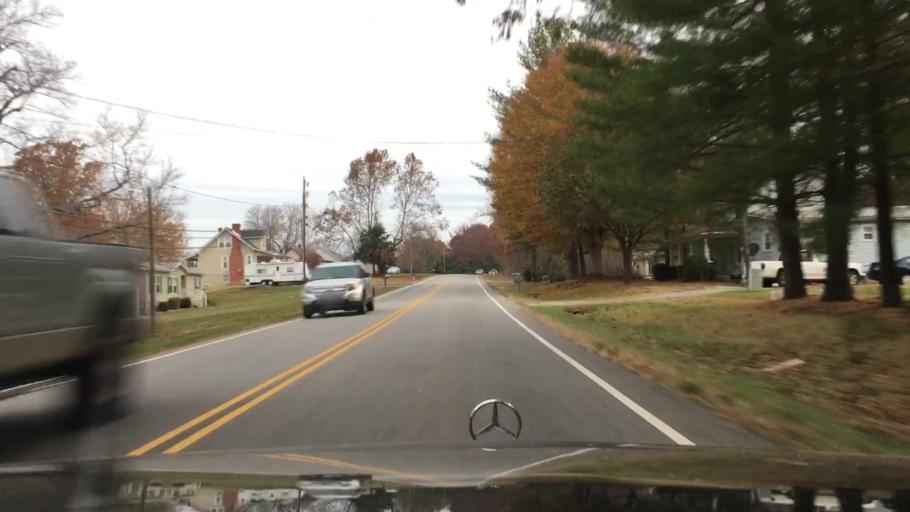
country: US
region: Virginia
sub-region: Campbell County
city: Altavista
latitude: 37.1340
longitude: -79.3068
